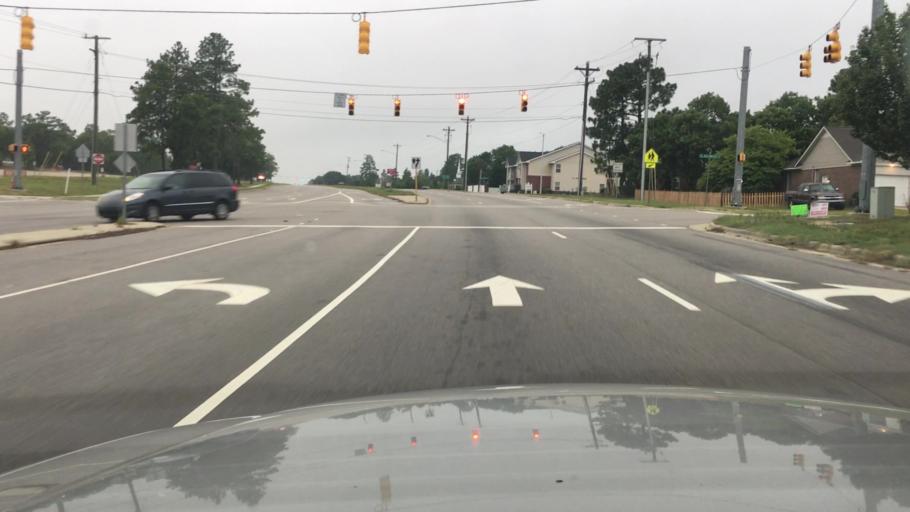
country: US
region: North Carolina
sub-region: Cumberland County
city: Hope Mills
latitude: 34.9779
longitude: -78.9237
